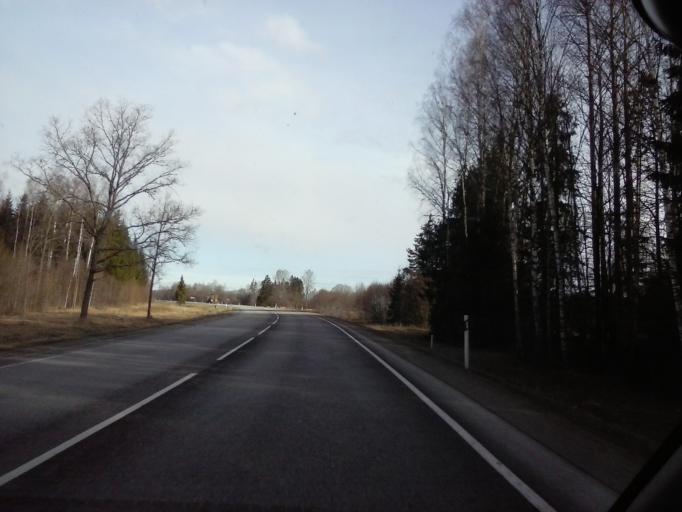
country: EE
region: Jaervamaa
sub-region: Paide linn
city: Paide
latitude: 58.8137
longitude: 25.7576
